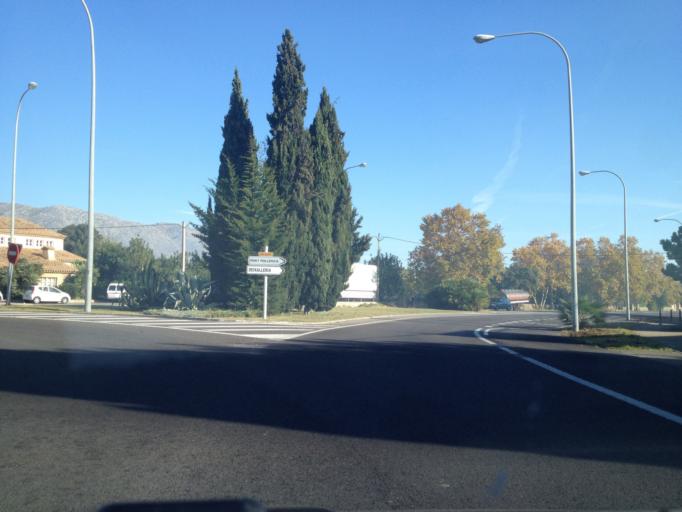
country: ES
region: Balearic Islands
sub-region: Illes Balears
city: Pollenca
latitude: 39.8844
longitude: 3.0226
